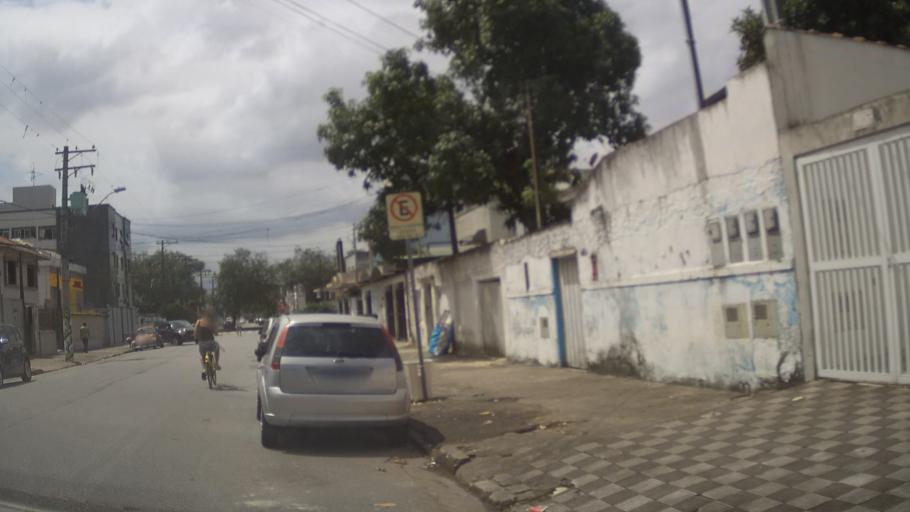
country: BR
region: Sao Paulo
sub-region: Santos
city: Santos
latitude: -23.9616
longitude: -46.3114
